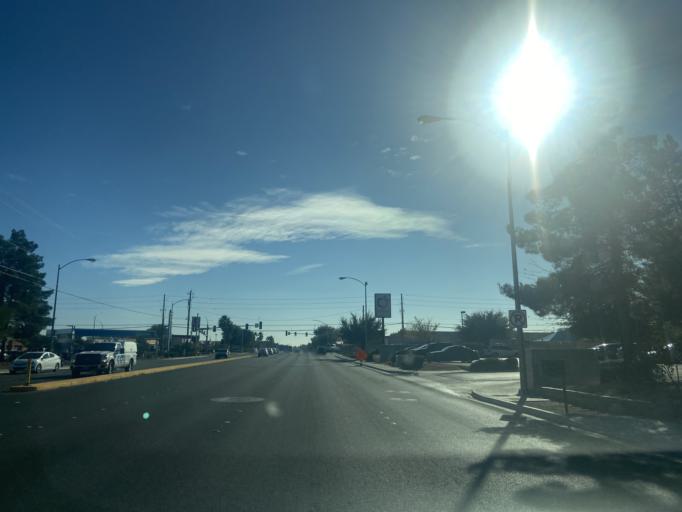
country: US
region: Nevada
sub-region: Clark County
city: North Las Vegas
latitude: 36.2409
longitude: -115.1802
